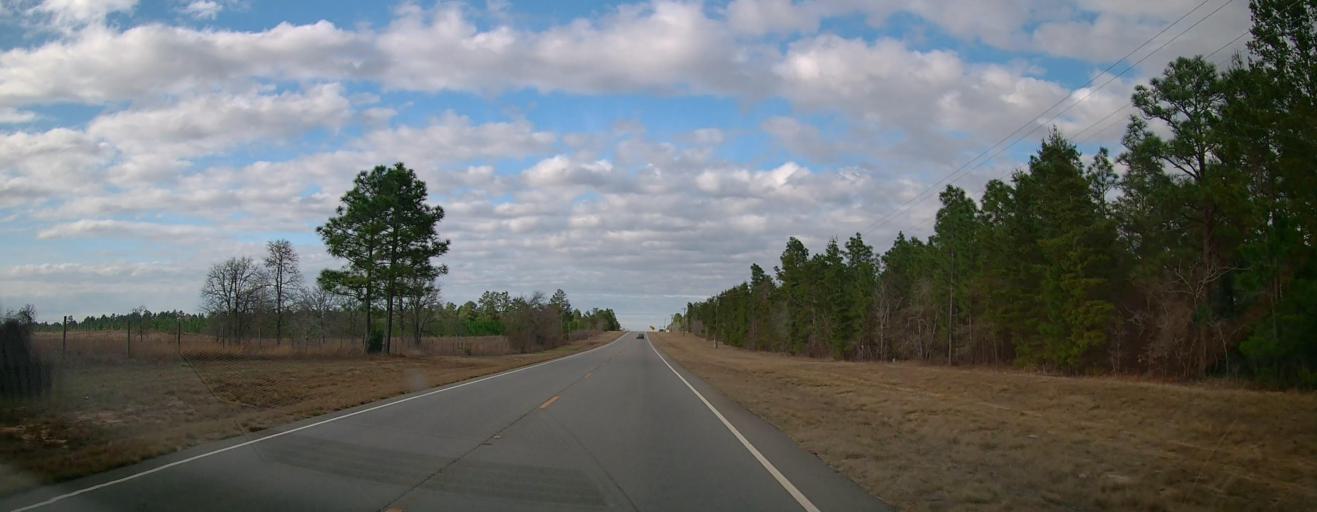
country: US
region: Georgia
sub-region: Marion County
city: Buena Vista
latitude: 32.4740
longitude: -84.5427
